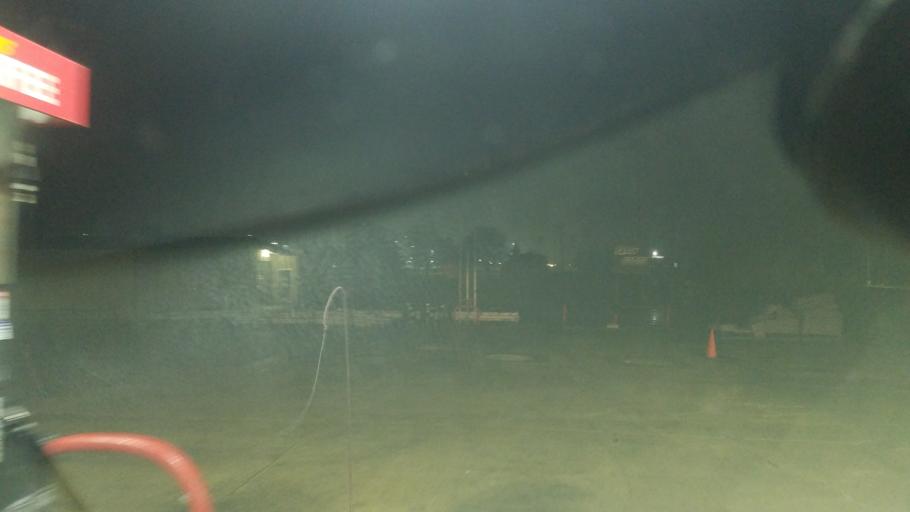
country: US
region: Michigan
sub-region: Gratiot County
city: Alma
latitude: 43.4066
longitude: -84.6664
